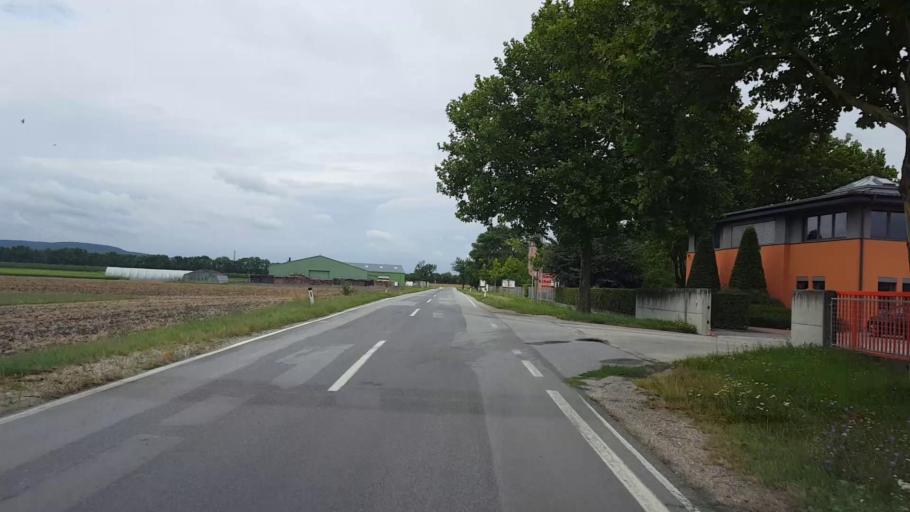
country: AT
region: Lower Austria
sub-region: Politischer Bezirk Bruck an der Leitha
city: Bruck an der Leitha
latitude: 48.0195
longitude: 16.7500
